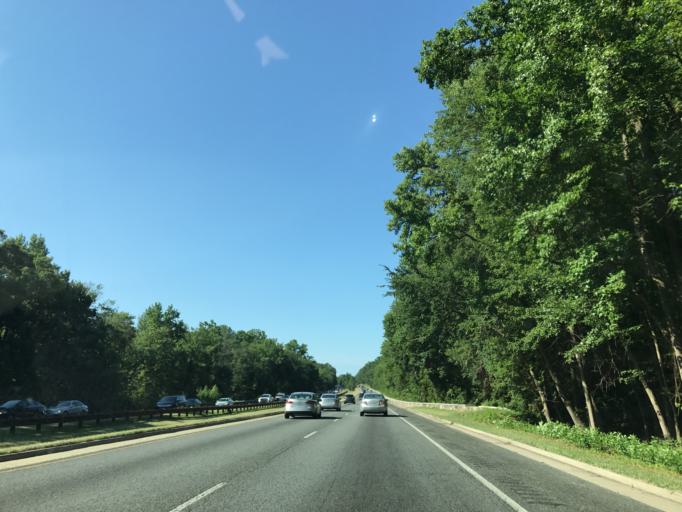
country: US
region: Maryland
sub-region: Prince George's County
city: Greenbelt
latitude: 39.0234
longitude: -76.8571
